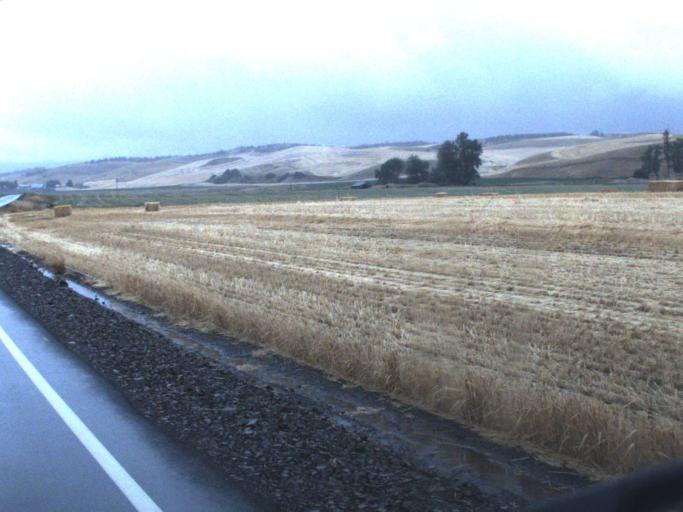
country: US
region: Washington
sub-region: Whitman County
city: Colfax
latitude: 47.0789
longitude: -117.5383
